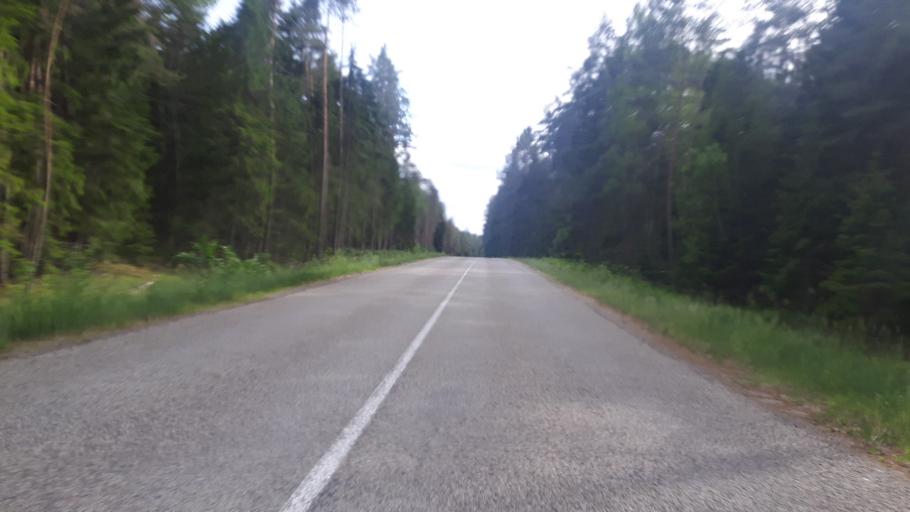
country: LV
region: Engure
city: Smarde
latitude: 57.0065
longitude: 23.3348
